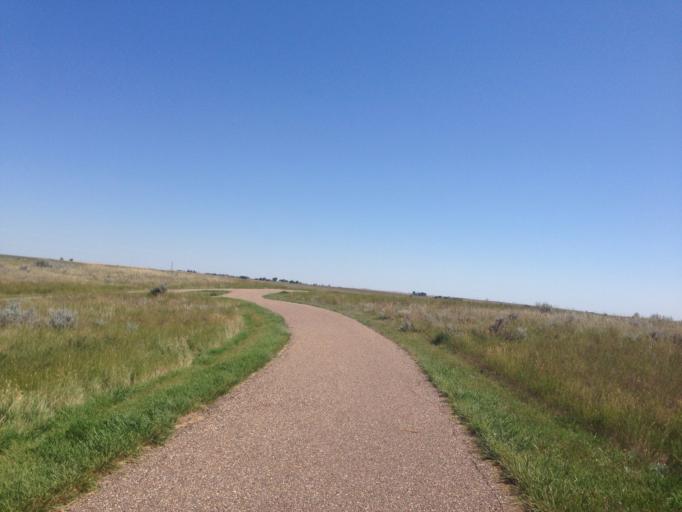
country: CA
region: Alberta
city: Medicine Hat
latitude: 50.0148
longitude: -110.6277
